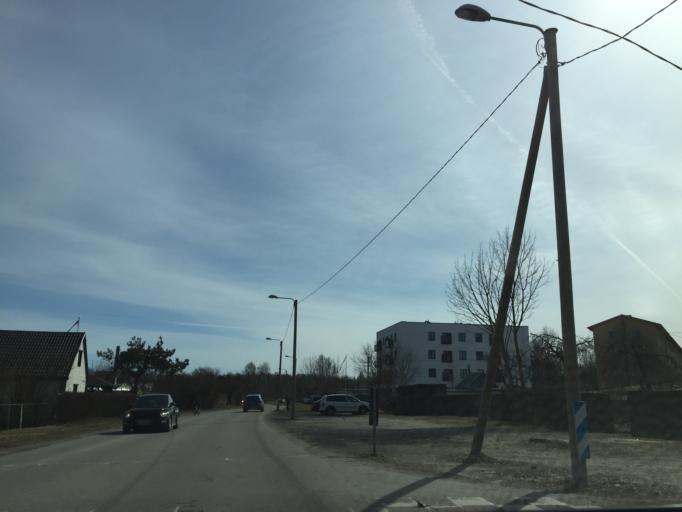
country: EE
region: Paernumaa
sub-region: Paernu linn
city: Parnu
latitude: 58.3821
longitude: 24.5292
